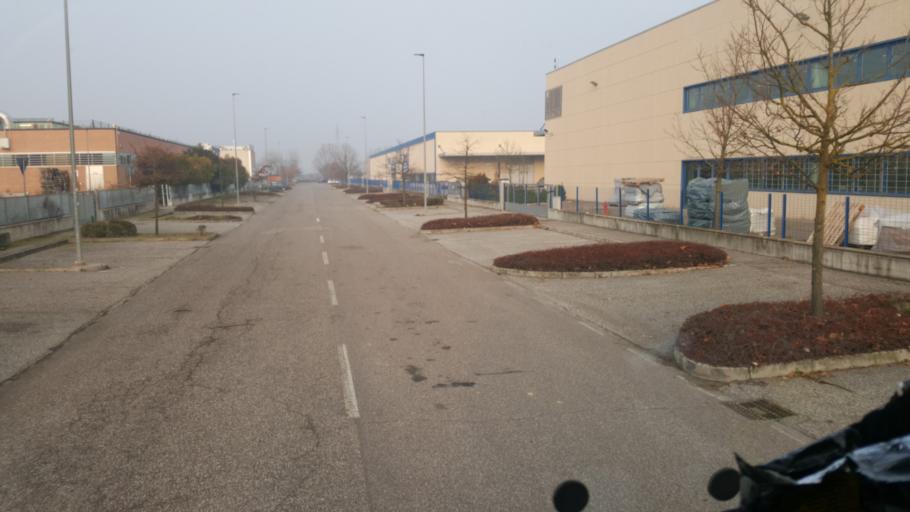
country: IT
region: Emilia-Romagna
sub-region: Provincia di Ravenna
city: Faenza
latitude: 44.3042
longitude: 11.8988
